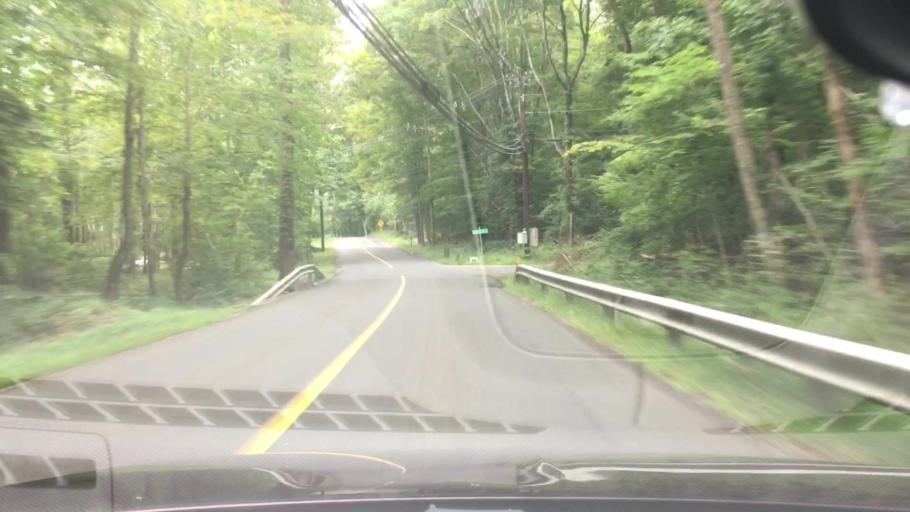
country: US
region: Connecticut
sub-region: New Haven County
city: Madison
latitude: 41.3361
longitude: -72.5808
